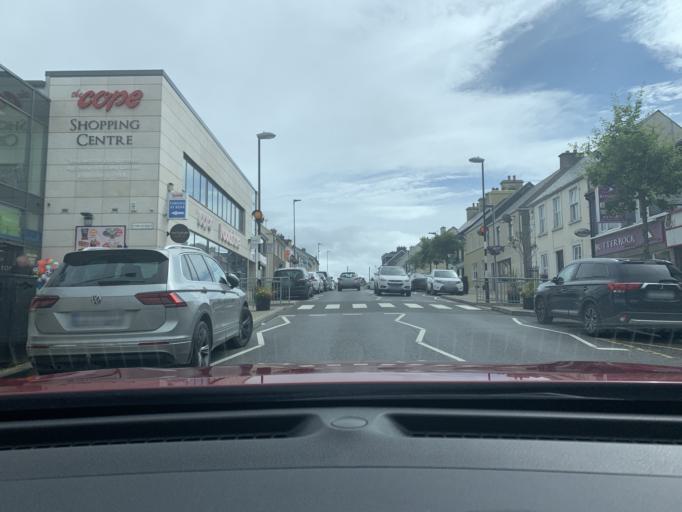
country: IE
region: Ulster
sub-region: County Donegal
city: Dungloe
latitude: 54.9490
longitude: -8.3601
